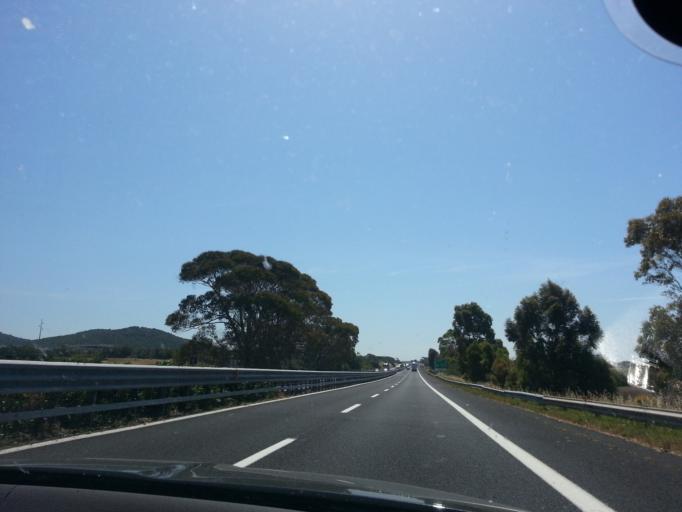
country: IT
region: Latium
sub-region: Citta metropolitana di Roma Capitale
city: Santa Marinella
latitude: 42.0423
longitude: 11.9290
